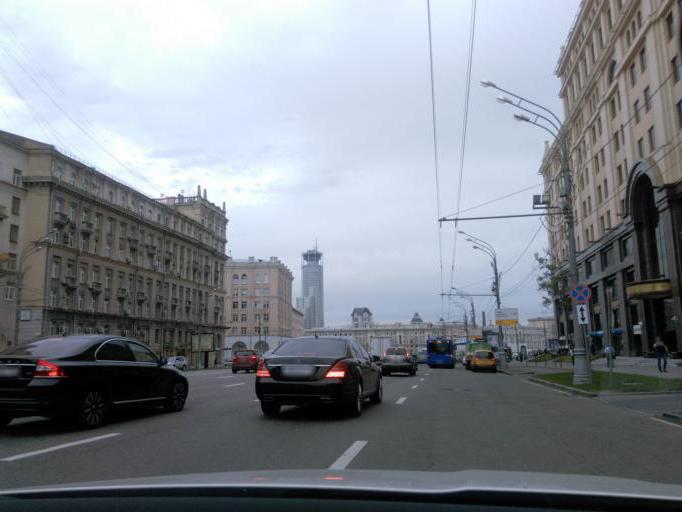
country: RU
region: Moscow
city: Zamoskvorech'ye
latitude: 55.7306
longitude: 37.6337
